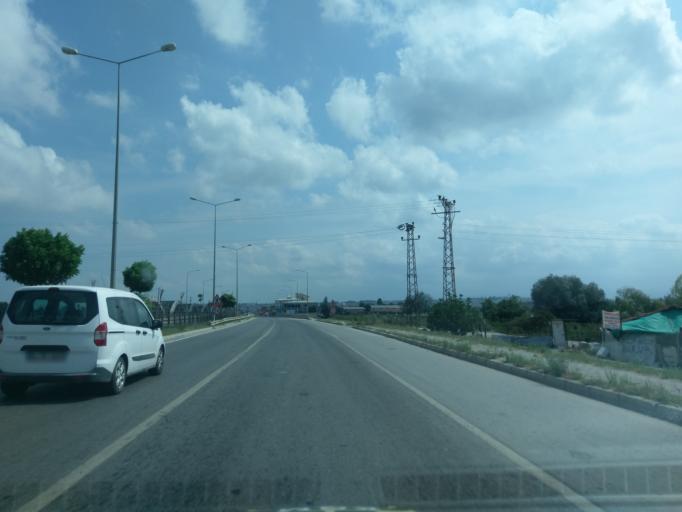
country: TR
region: Samsun
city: Bafra
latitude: 41.5683
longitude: 35.8790
